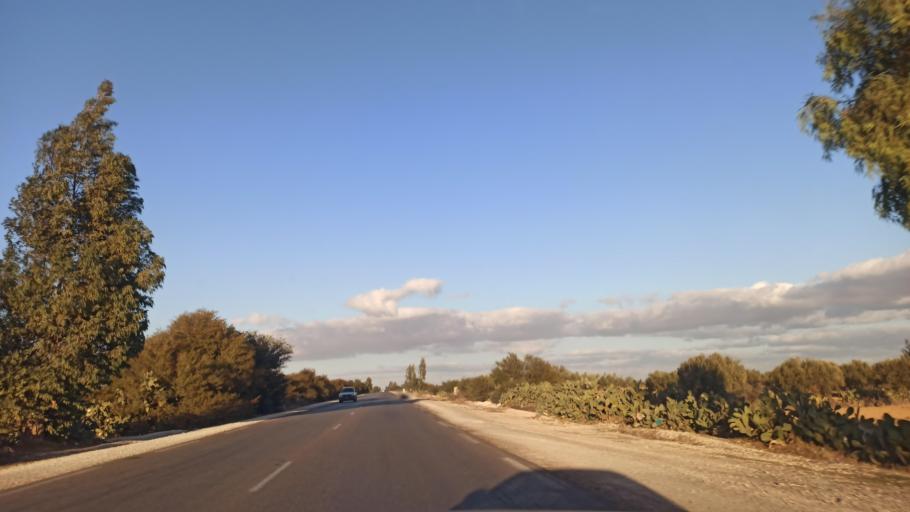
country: TN
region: Al Qayrawan
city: Sbikha
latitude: 35.8608
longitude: 10.2064
